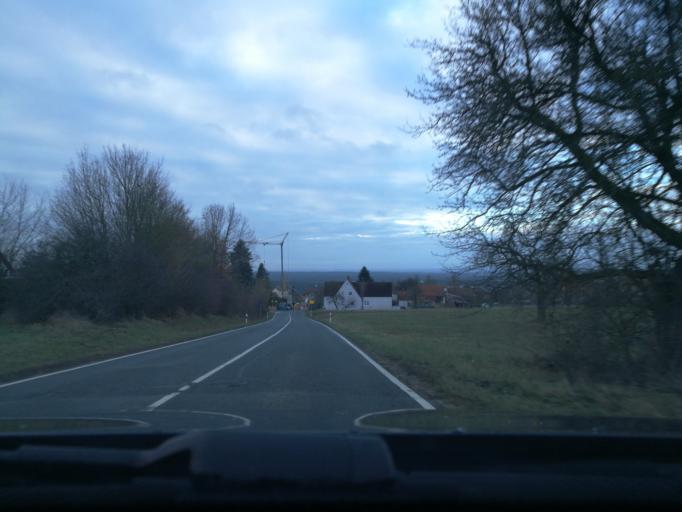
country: DE
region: Bavaria
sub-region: Regierungsbezirk Mittelfranken
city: Marloffstein
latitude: 49.6208
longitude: 11.0653
